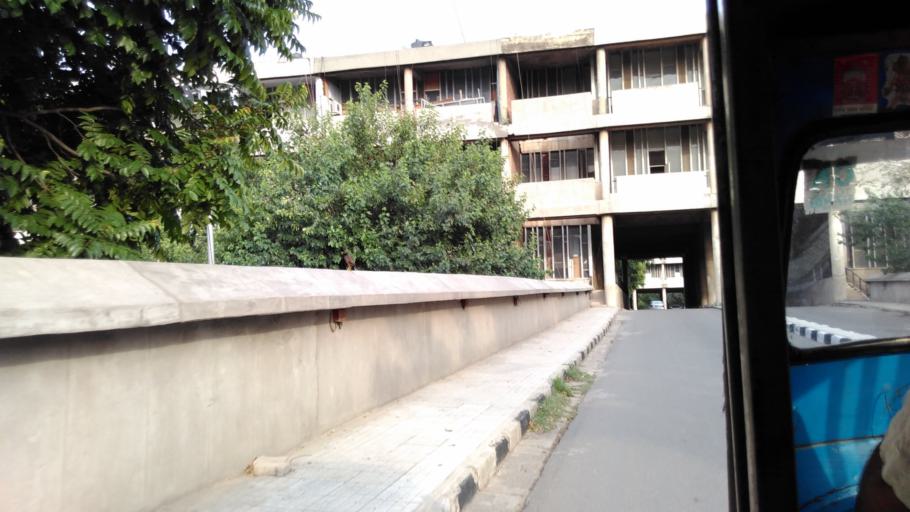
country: IN
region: Chandigarh
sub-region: Chandigarh
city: Chandigarh
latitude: 30.7419
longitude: 76.7824
